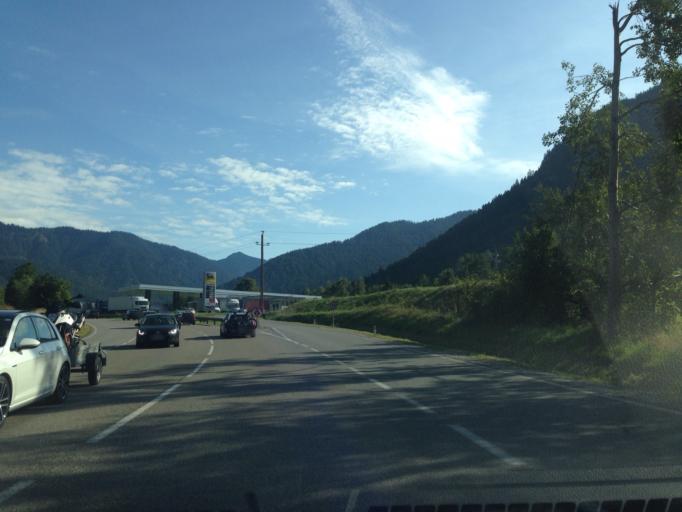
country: AT
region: Tyrol
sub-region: Politischer Bezirk Reutte
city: Breitenwang
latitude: 47.4792
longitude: 10.7336
